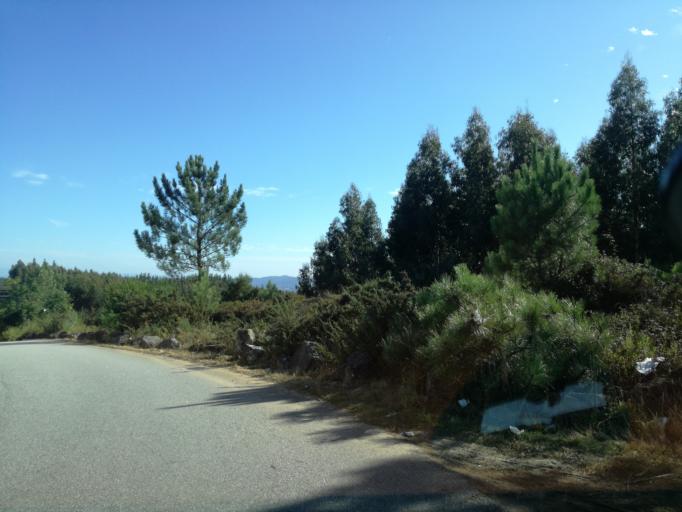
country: PT
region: Porto
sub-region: Pacos de Ferreira
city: Seroa
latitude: 41.2621
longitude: -8.4505
